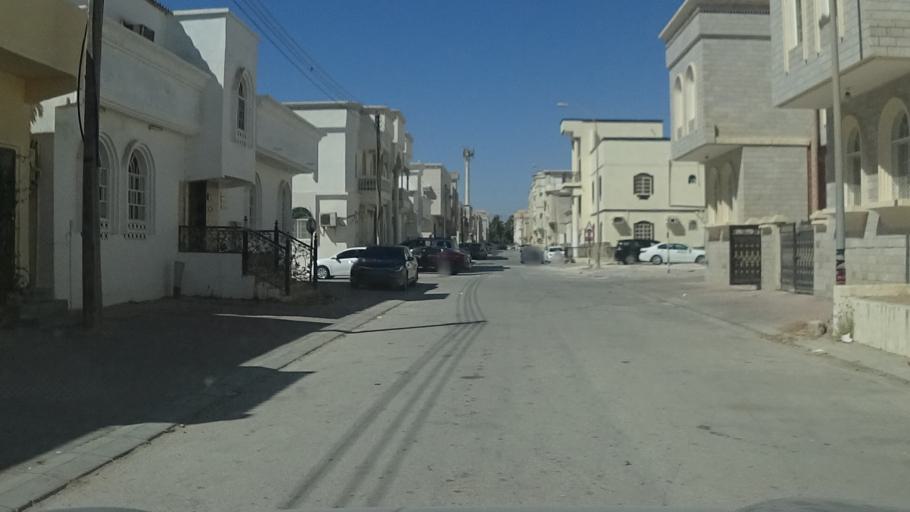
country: OM
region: Zufar
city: Salalah
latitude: 17.0252
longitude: 54.1603
